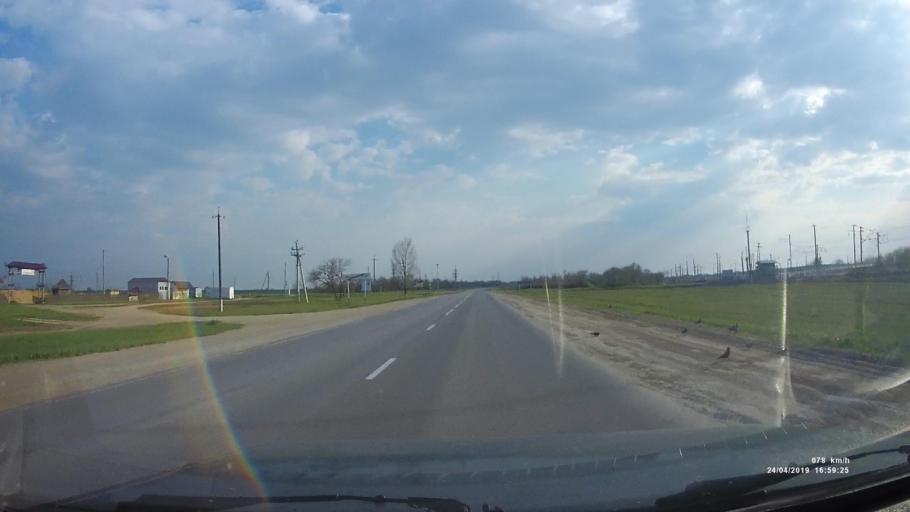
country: RU
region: Rostov
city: Proletarsk
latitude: 46.6182
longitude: 41.6504
